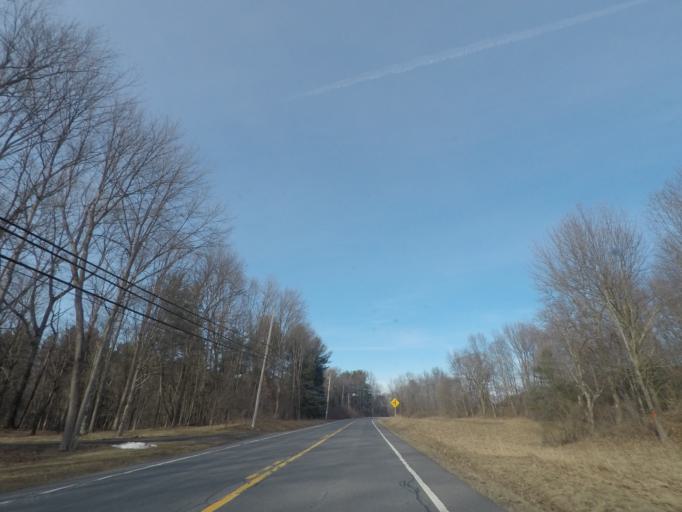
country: US
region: New York
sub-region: Rensselaer County
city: Nassau
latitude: 42.4914
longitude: -73.6247
